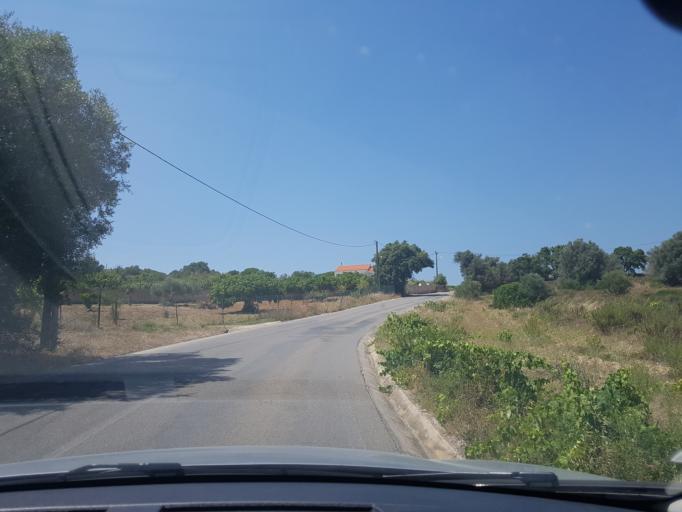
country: PT
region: Faro
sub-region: Lagoa
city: Carvoeiro
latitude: 37.1048
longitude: -8.4300
